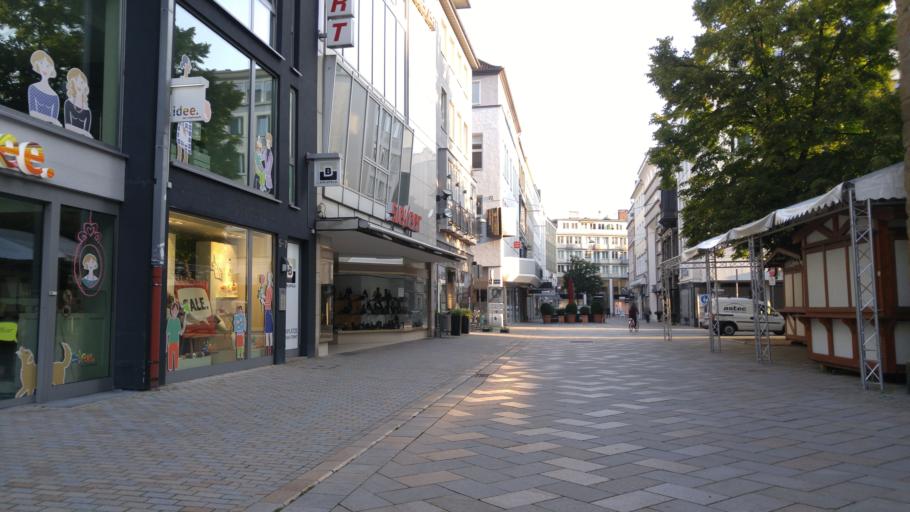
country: DE
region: North Rhine-Westphalia
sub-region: Regierungsbezirk Detmold
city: Bielefeld
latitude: 52.0210
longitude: 8.5318
